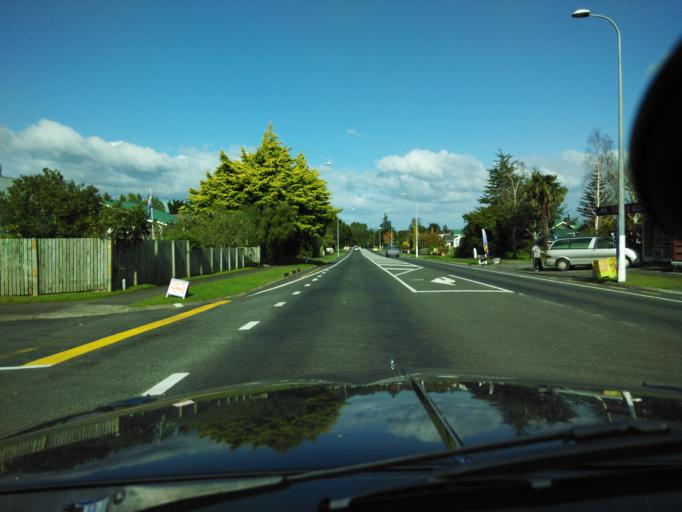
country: NZ
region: Waikato
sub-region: Hauraki District
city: Paeroa
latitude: -37.5339
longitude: 175.7076
